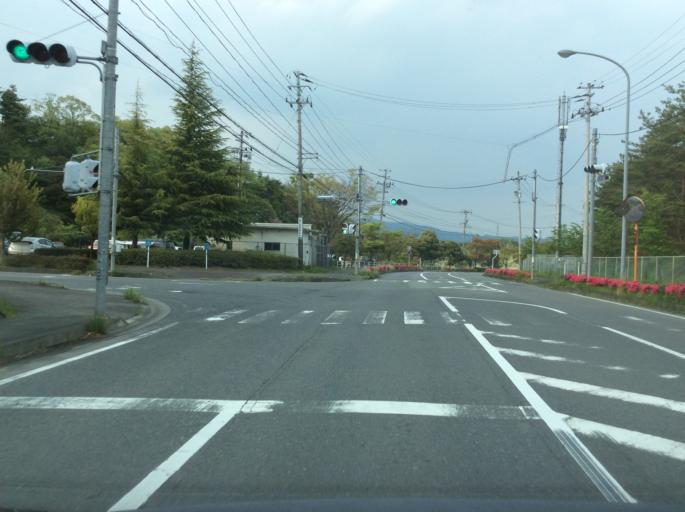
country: JP
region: Fukushima
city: Iwaki
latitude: 37.0766
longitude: 140.8439
